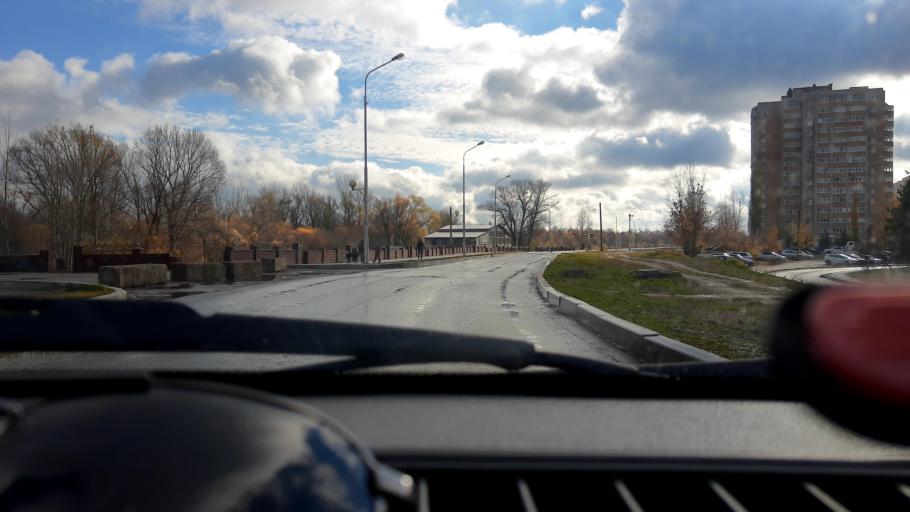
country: RU
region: Bashkortostan
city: Ufa
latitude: 54.7749
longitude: 56.0848
